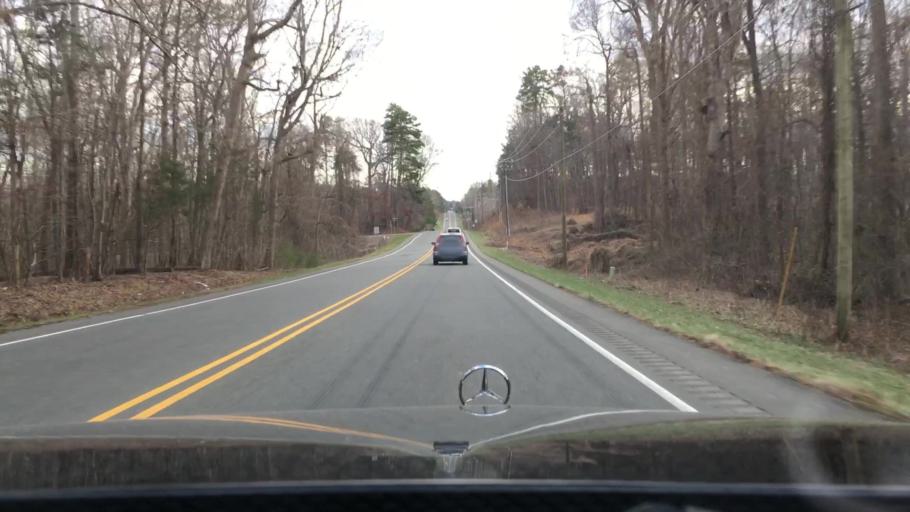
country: US
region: North Carolina
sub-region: Orange County
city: Hillsborough
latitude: 36.1021
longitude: -79.1080
